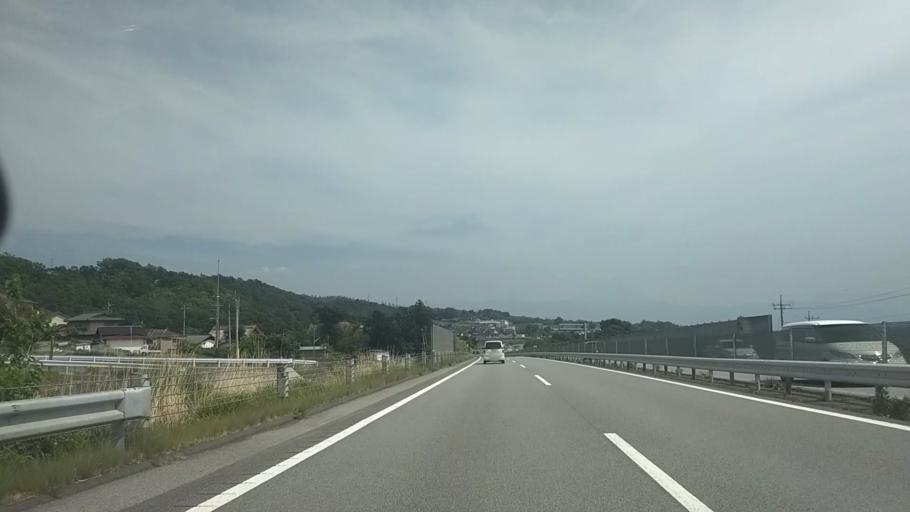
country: JP
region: Yamanashi
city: Nirasaki
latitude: 35.7588
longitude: 138.4357
